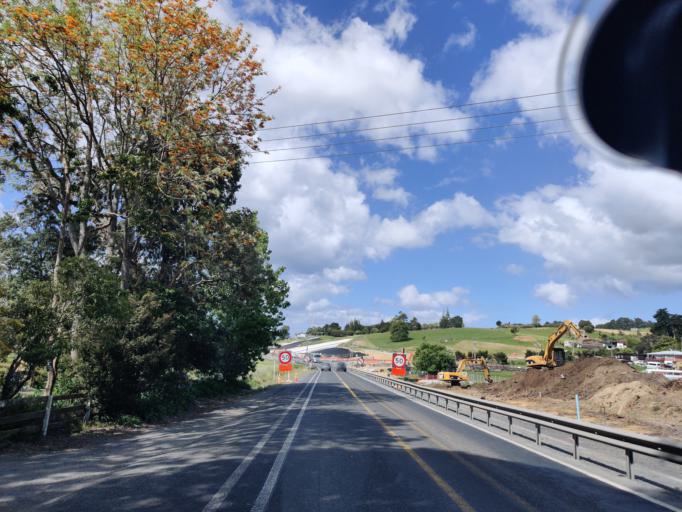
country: NZ
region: Northland
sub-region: Whangarei
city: Whangarei
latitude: -35.7908
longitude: 174.3007
